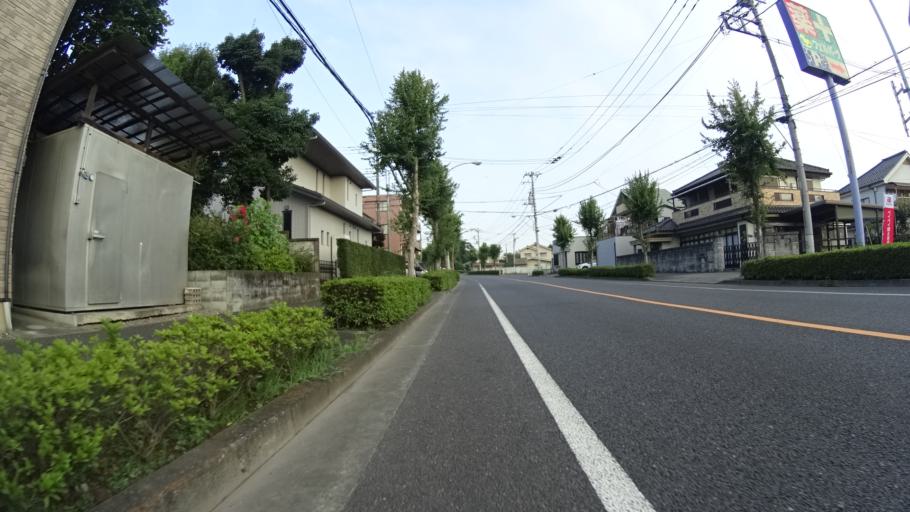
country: JP
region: Tokyo
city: Ome
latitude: 35.7736
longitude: 139.2836
